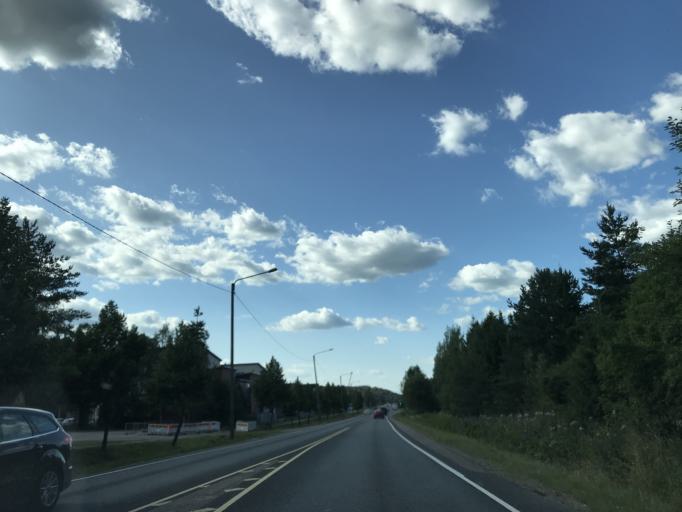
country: FI
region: Uusimaa
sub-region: Helsinki
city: Nurmijaervi
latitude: 60.4610
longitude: 24.8145
